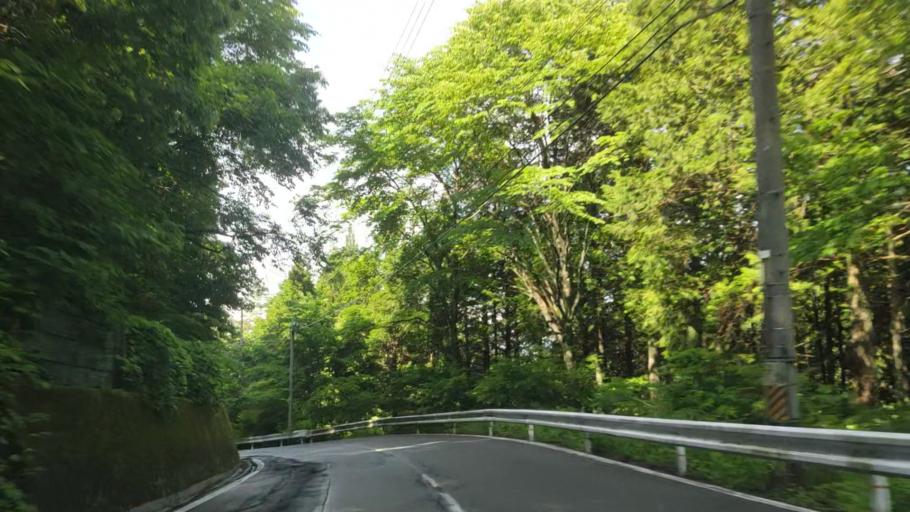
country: JP
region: Nagano
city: Suwa
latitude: 36.0768
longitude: 138.1388
